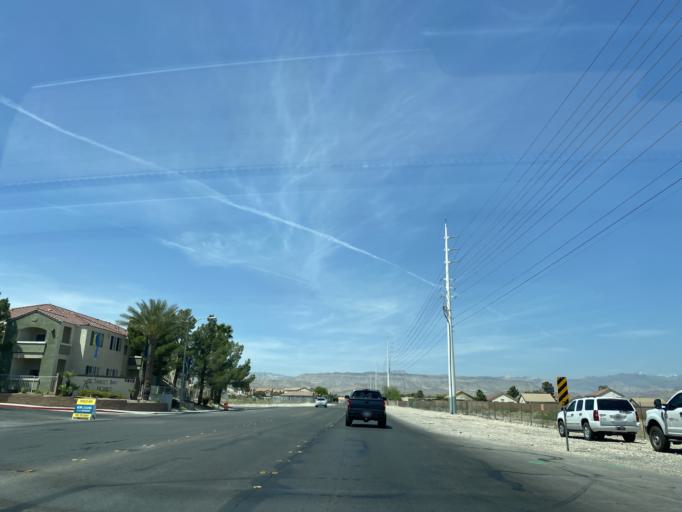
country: US
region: Nevada
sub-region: Clark County
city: Spring Valley
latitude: 36.0852
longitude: -115.2530
